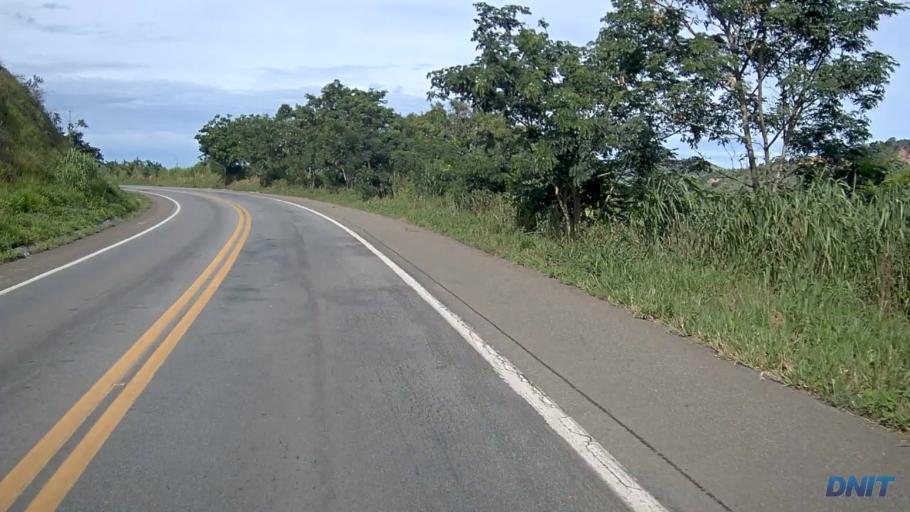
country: BR
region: Minas Gerais
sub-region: Belo Oriente
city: Belo Oriente
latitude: -19.1718
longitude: -42.2499
